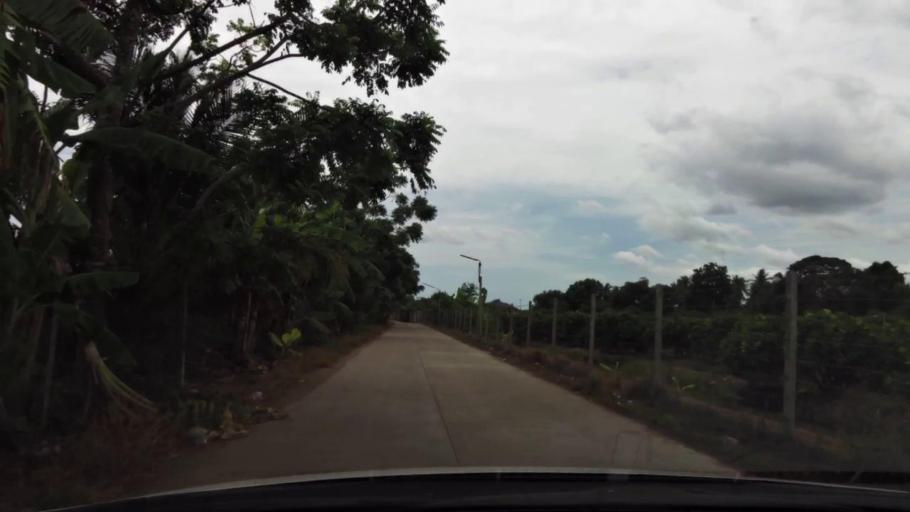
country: TH
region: Samut Sakhon
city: Ban Phaeo
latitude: 13.5587
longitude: 100.0400
